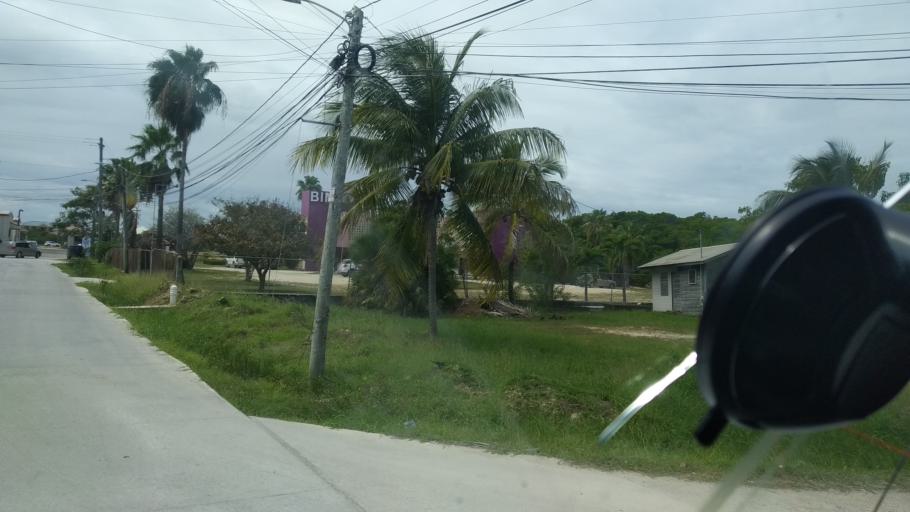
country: BZ
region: Belize
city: Belize City
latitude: 17.5130
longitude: -88.2024
